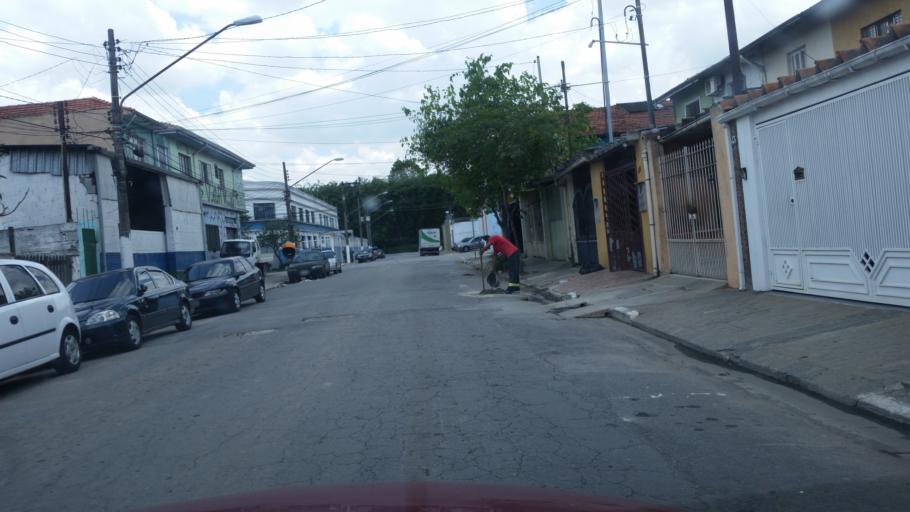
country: BR
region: Sao Paulo
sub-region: Diadema
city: Diadema
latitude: -23.6639
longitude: -46.7068
